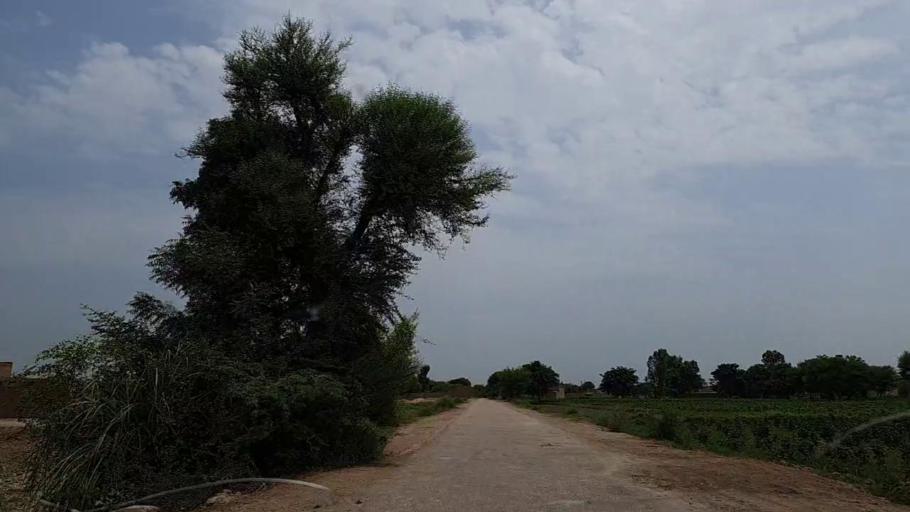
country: PK
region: Sindh
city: Tharu Shah
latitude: 26.9105
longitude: 68.0941
